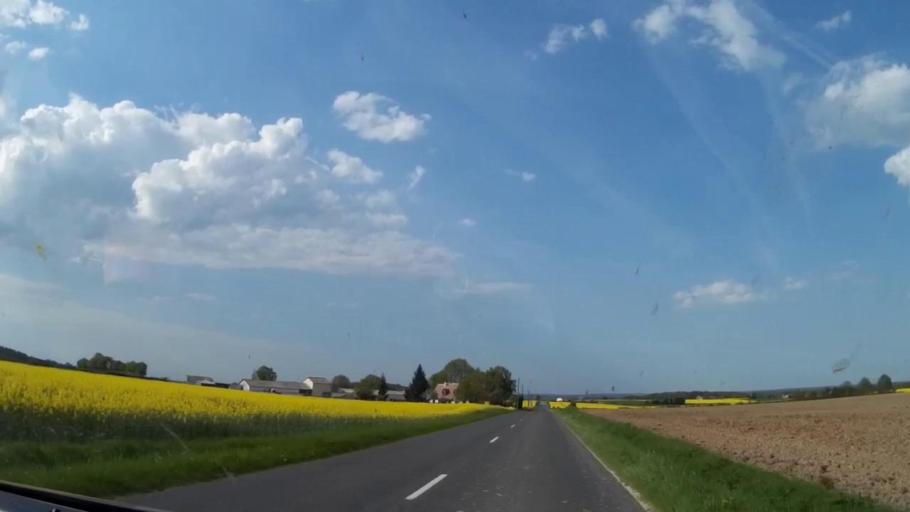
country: FR
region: Centre
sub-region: Departement du Loir-et-Cher
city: Mondoubleau
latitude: 47.9502
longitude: 0.9320
